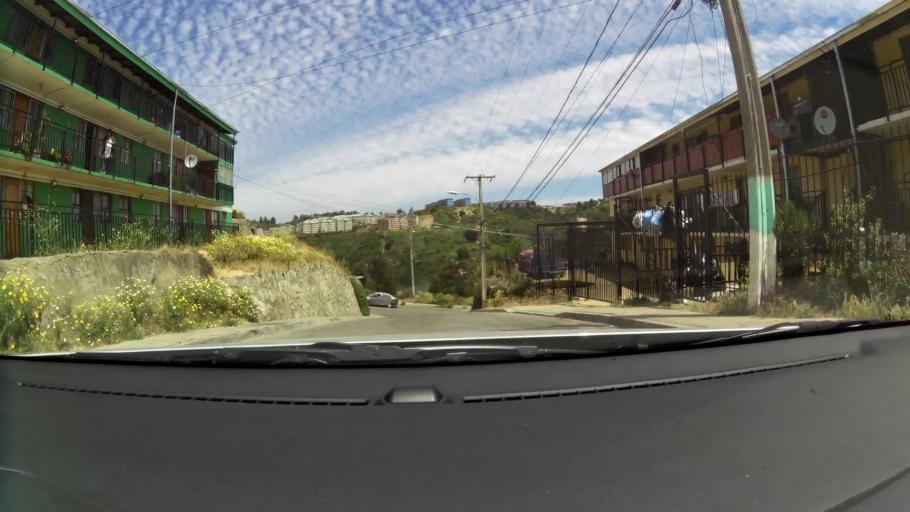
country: CL
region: Valparaiso
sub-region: Provincia de Valparaiso
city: Vina del Mar
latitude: -33.0572
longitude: -71.5670
